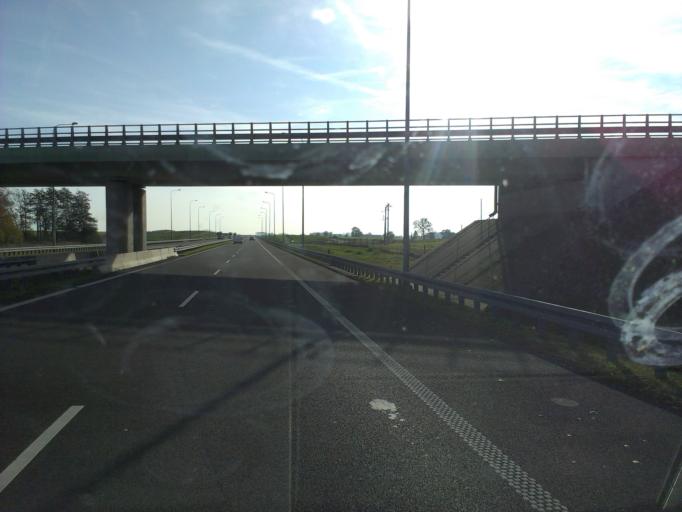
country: PL
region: West Pomeranian Voivodeship
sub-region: Powiat pyrzycki
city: Kozielice
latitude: 53.1194
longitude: 14.7438
